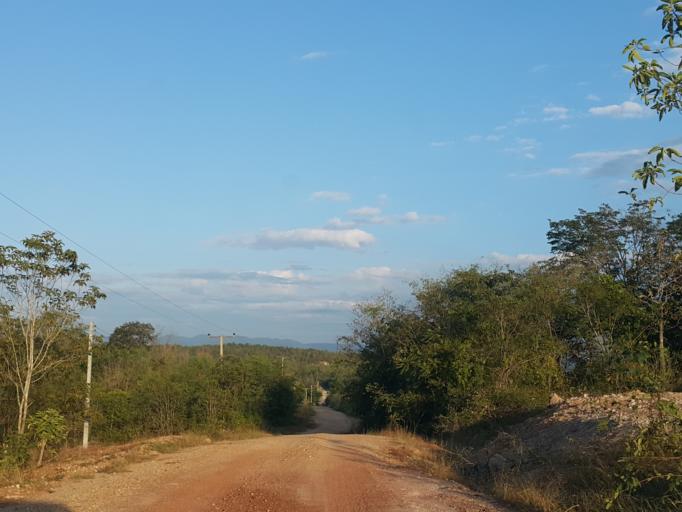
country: TH
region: Lampang
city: Lampang
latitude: 18.4335
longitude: 99.5835
